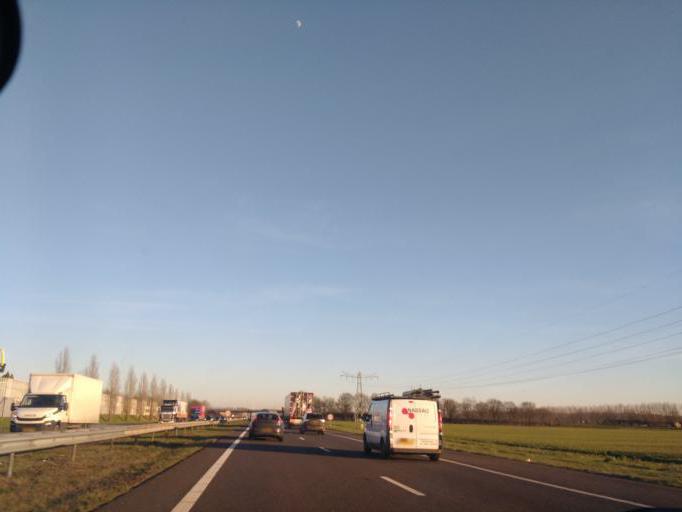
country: NL
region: Gelderland
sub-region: Gemeente Beuningen
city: Beuningen
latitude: 51.8499
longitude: 5.7522
